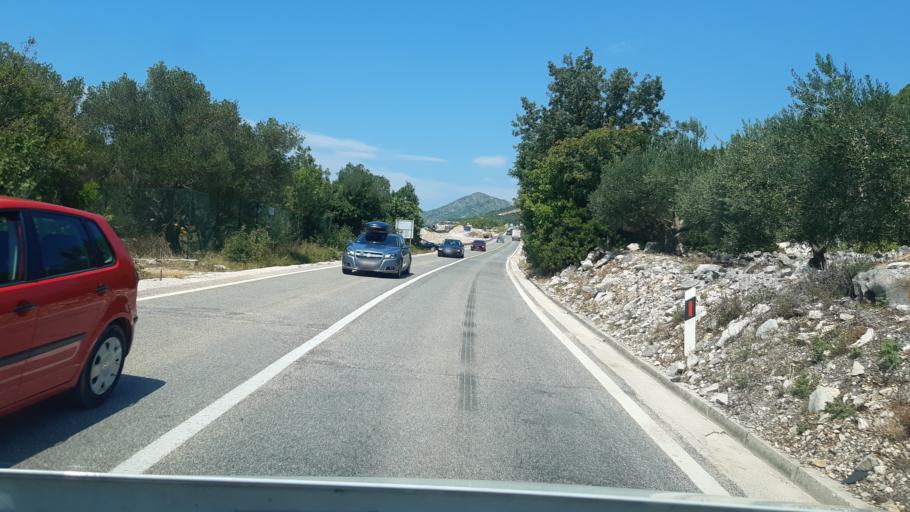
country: HR
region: Dubrovacko-Neretvanska
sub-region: Grad Dubrovnik
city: Opuzen
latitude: 42.9489
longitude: 17.5330
